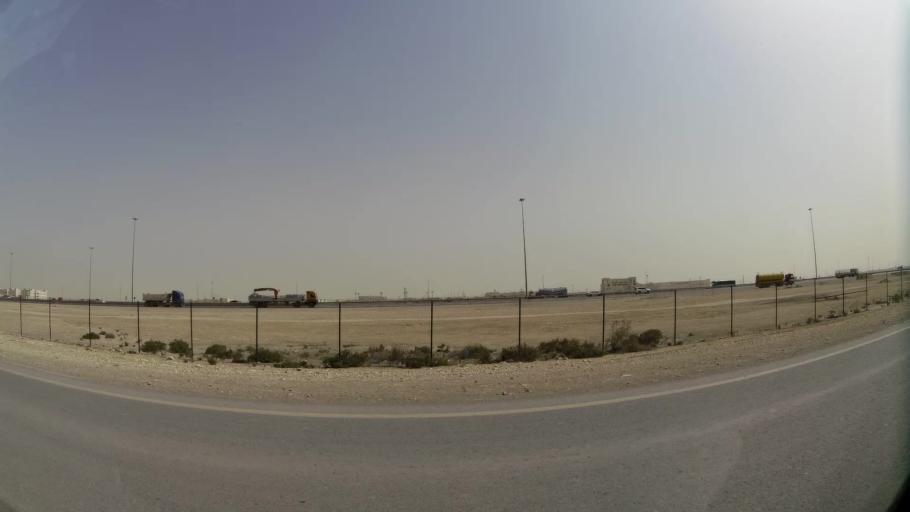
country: QA
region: Baladiyat ar Rayyan
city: Ar Rayyan
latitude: 25.1855
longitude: 51.3591
